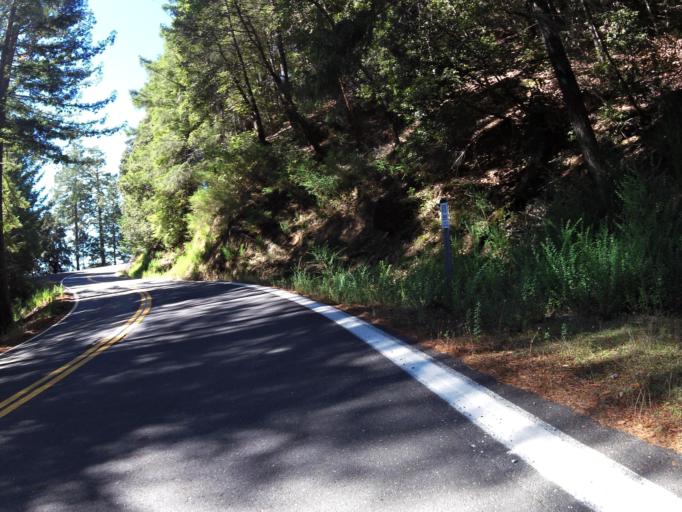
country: US
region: California
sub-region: Humboldt County
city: Redway
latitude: 39.8496
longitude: -123.7386
